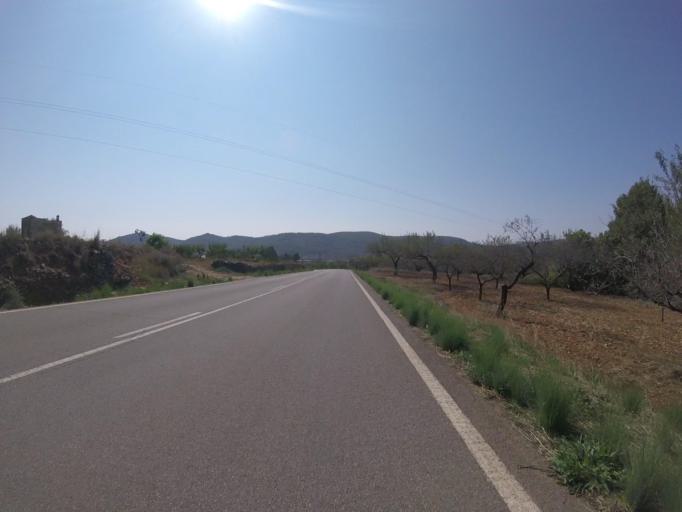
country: ES
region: Valencia
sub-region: Provincia de Castello
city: Adzaneta
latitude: 40.2284
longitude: -0.1747
